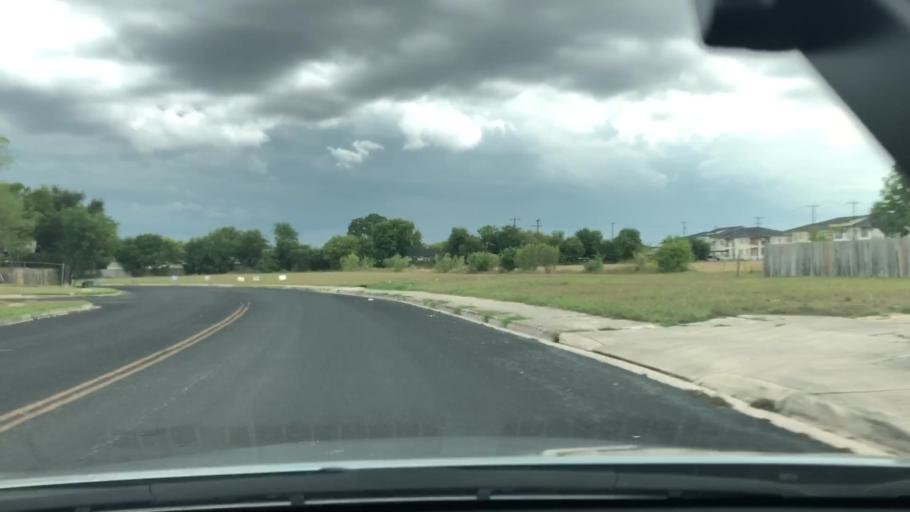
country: US
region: Texas
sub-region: Bexar County
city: Kirby
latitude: 29.4779
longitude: -98.3578
